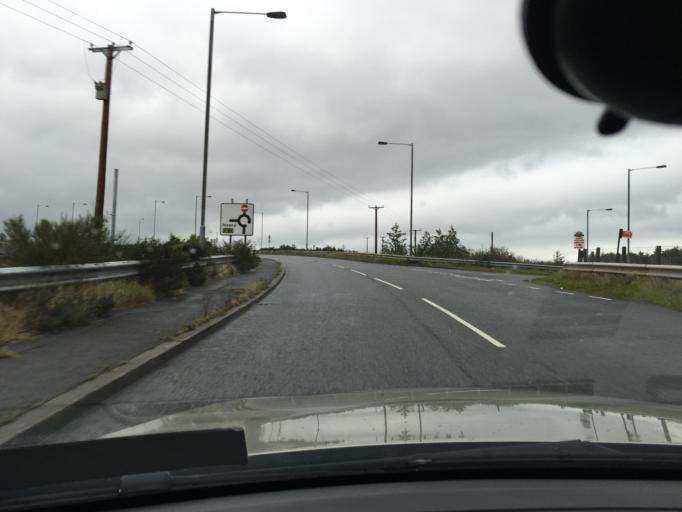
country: GB
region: Northern Ireland
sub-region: Newry and Mourne District
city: Newry
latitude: 54.1367
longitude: -6.3424
